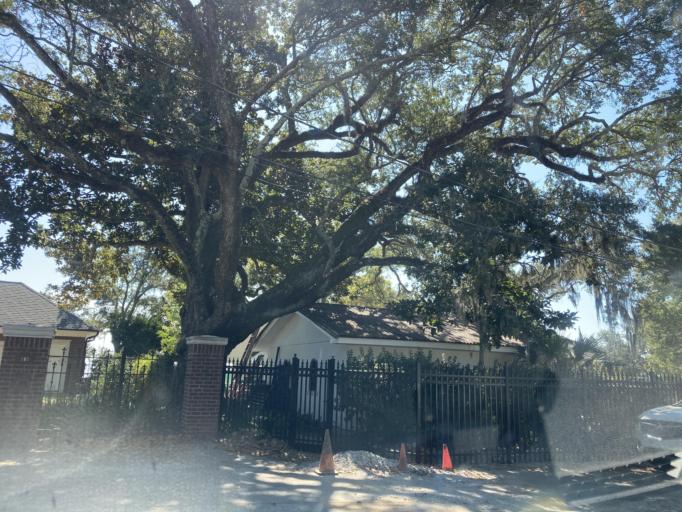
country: US
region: Mississippi
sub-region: Jackson County
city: Ocean Springs
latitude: 30.4105
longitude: -88.8386
